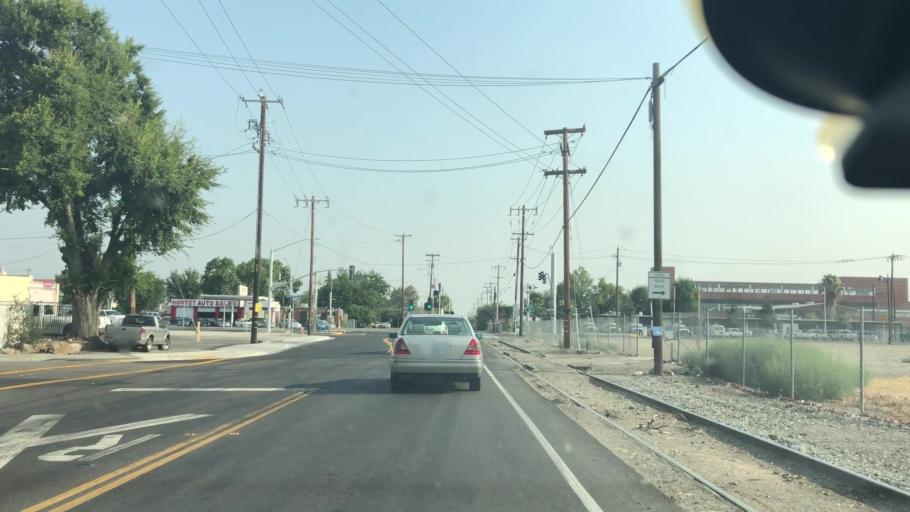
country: US
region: California
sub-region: San Joaquin County
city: Tracy
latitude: 37.7387
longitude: -121.4165
